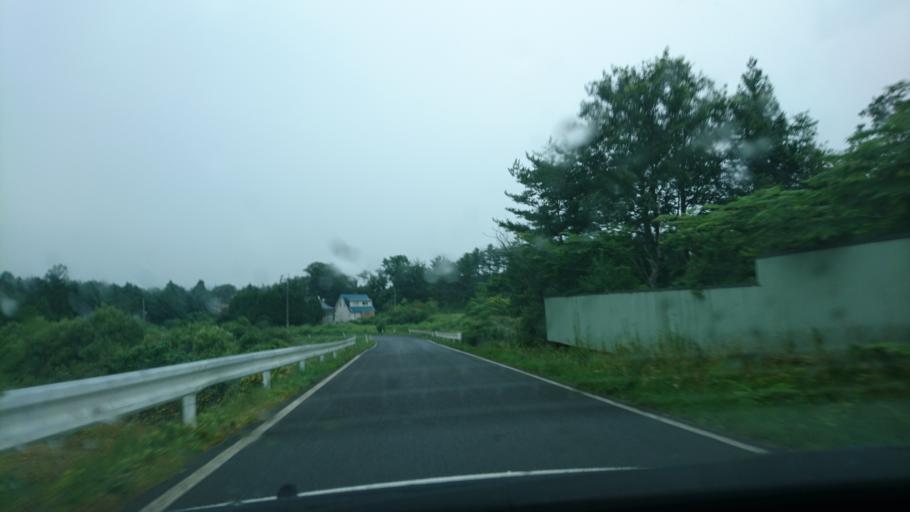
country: JP
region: Iwate
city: Ichinoseki
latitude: 38.9076
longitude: 141.1983
